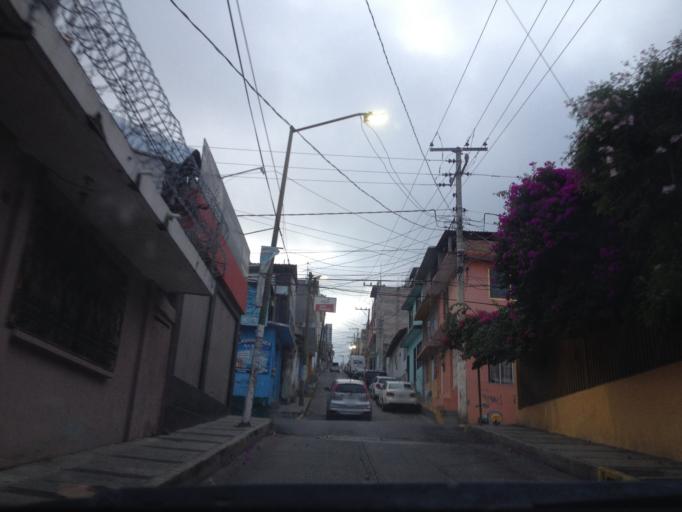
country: MX
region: Guerrero
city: Chilpancingo de los Bravos
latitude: 17.5553
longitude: -99.5023
